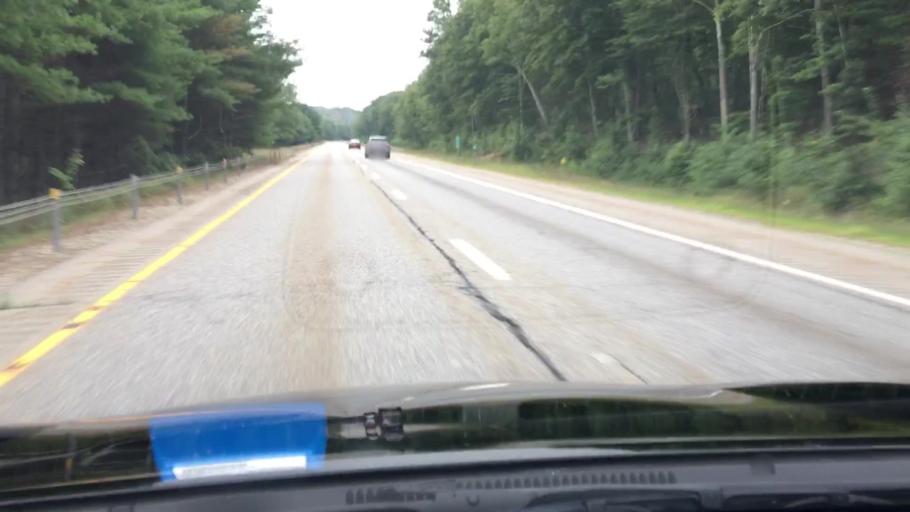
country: US
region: Connecticut
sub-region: Windham County
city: Thompson
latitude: 41.9920
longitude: -71.8531
